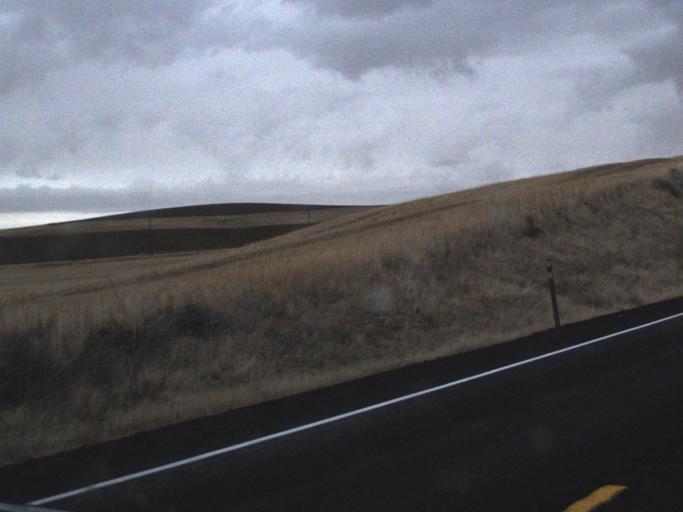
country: US
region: Washington
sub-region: Garfield County
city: Pomeroy
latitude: 46.8042
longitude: -117.8372
